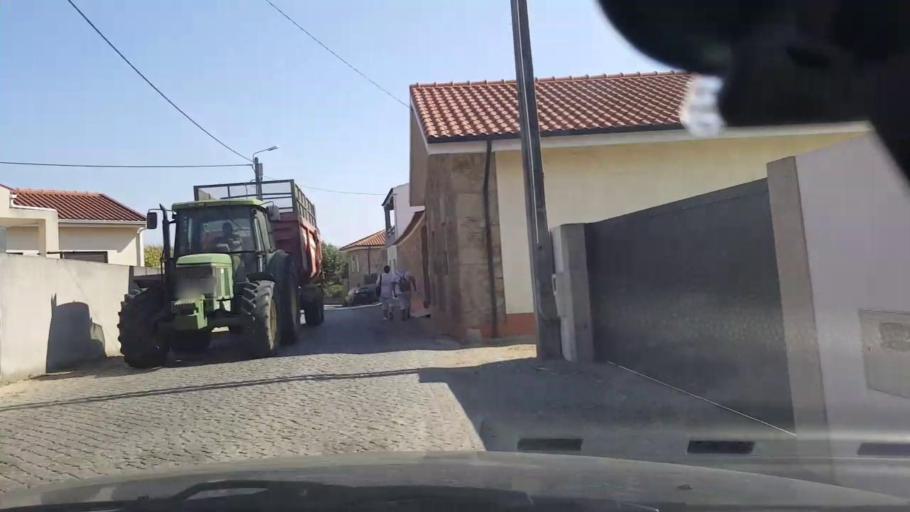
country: PT
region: Porto
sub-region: Povoa de Varzim
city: Pedroso
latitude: 41.4108
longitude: -8.6954
